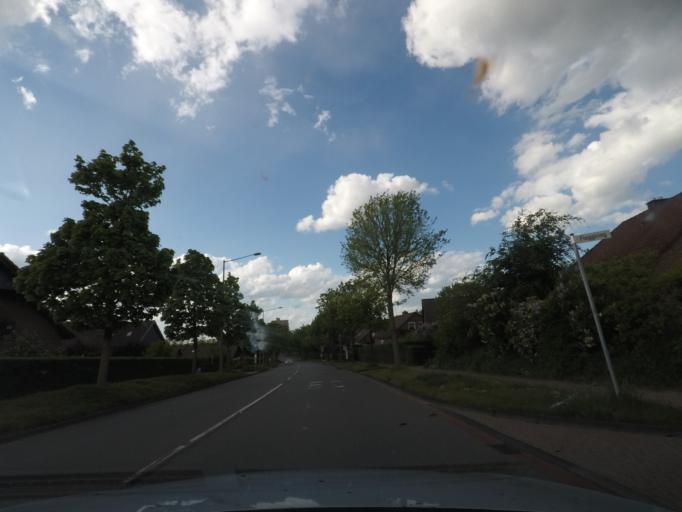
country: DE
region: Lower Saxony
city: Helmstedt
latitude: 52.2188
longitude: 11.0350
